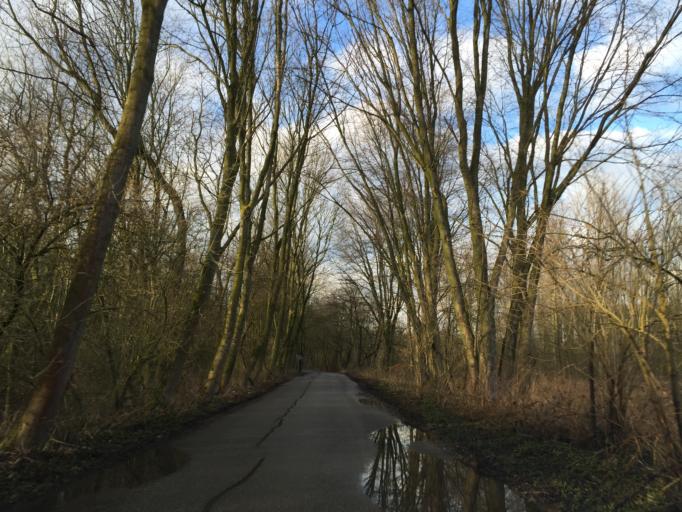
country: NL
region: South Holland
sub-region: Gemeente Den Haag
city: Ypenburg
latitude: 52.0224
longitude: 4.3872
